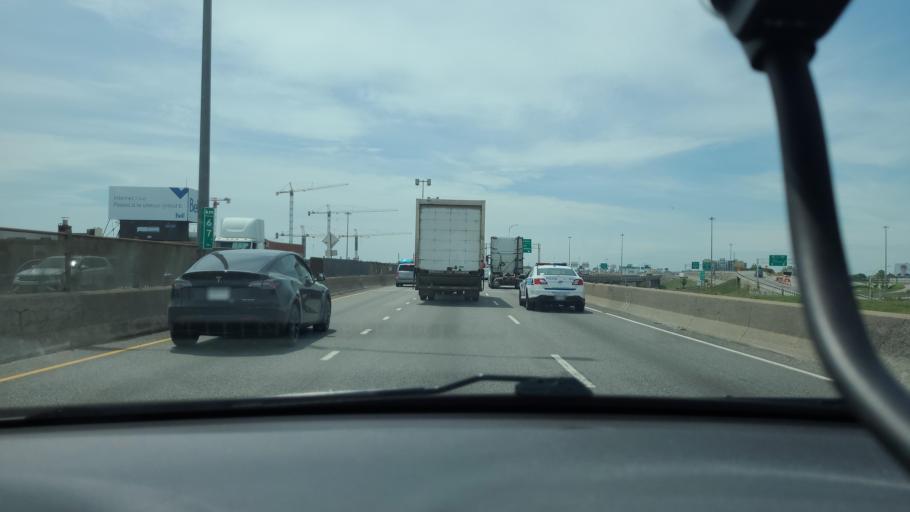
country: CA
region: Quebec
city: Saint-Laurent
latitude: 45.5059
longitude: -73.6629
